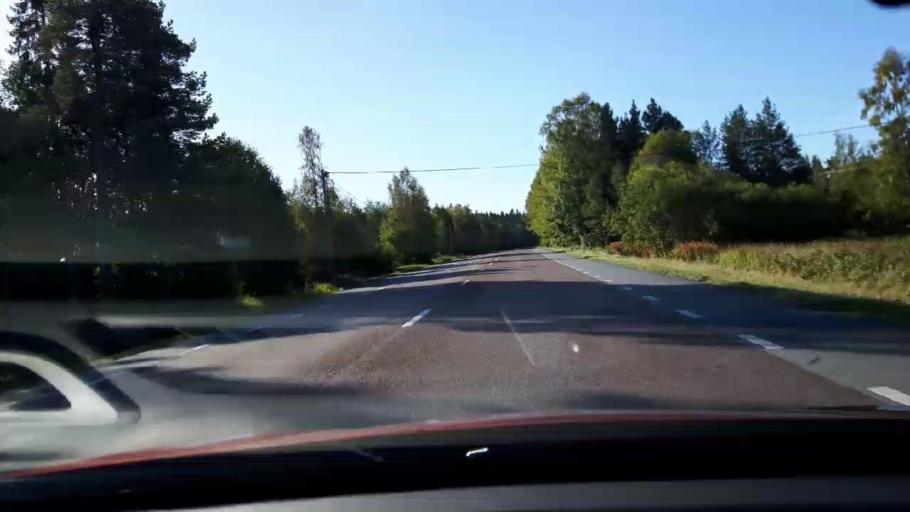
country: SE
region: Jaemtland
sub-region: Braecke Kommun
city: Braecke
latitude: 62.9063
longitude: 15.2642
